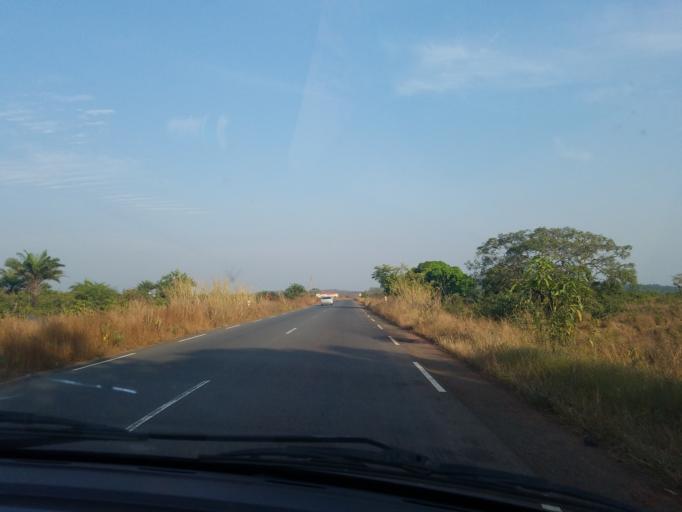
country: GN
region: Boke
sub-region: Boffa
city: Boffa
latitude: 10.3519
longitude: -14.2561
